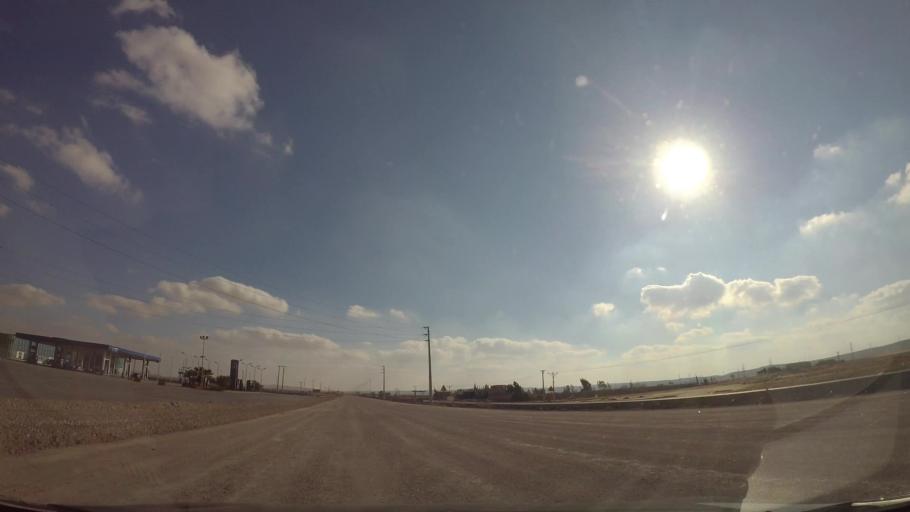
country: JO
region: Karak
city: Adir
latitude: 31.2768
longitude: 36.0540
